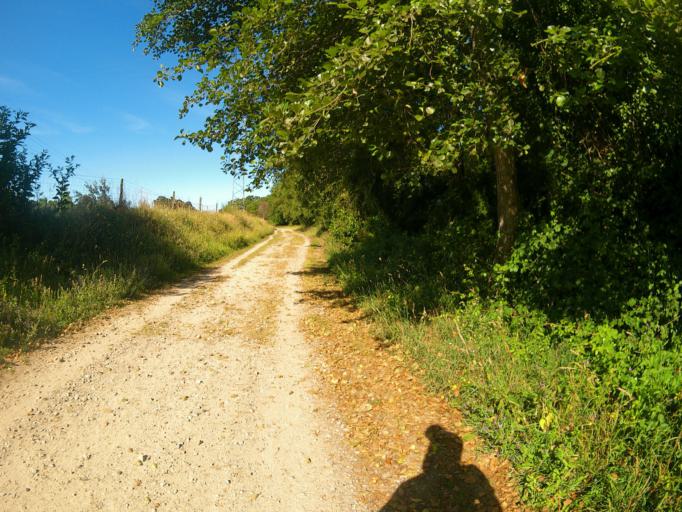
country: PT
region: Viana do Castelo
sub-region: Ponte de Lima
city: Ponte de Lima
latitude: 41.7384
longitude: -8.6477
